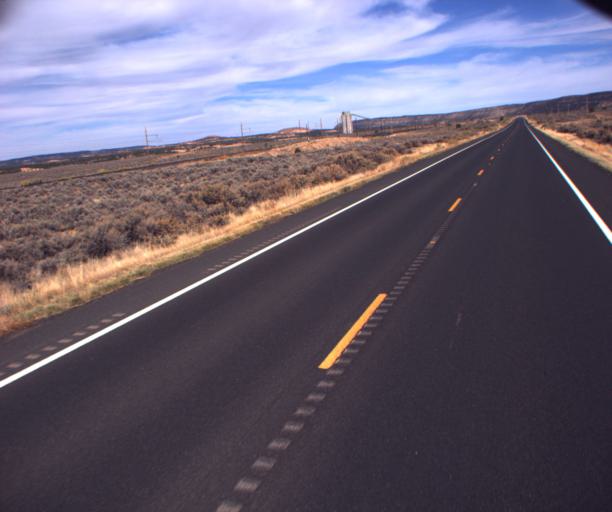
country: US
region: Arizona
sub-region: Navajo County
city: Kayenta
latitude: 36.5461
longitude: -110.5371
